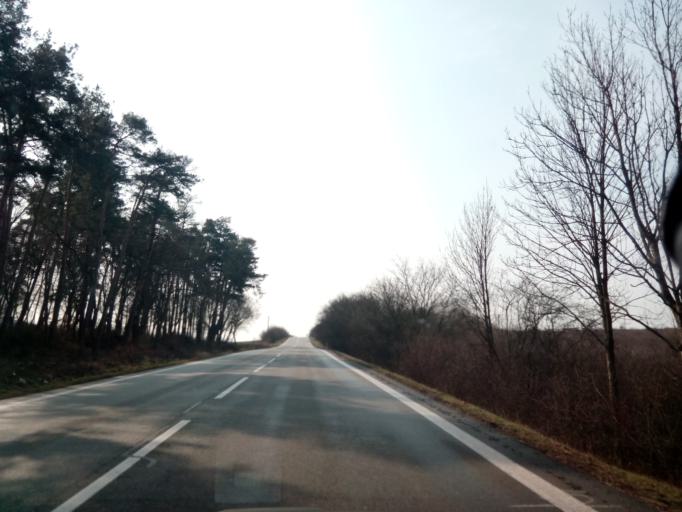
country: HU
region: Borsod-Abauj-Zemplen
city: Satoraljaujhely
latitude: 48.5156
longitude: 21.6586
